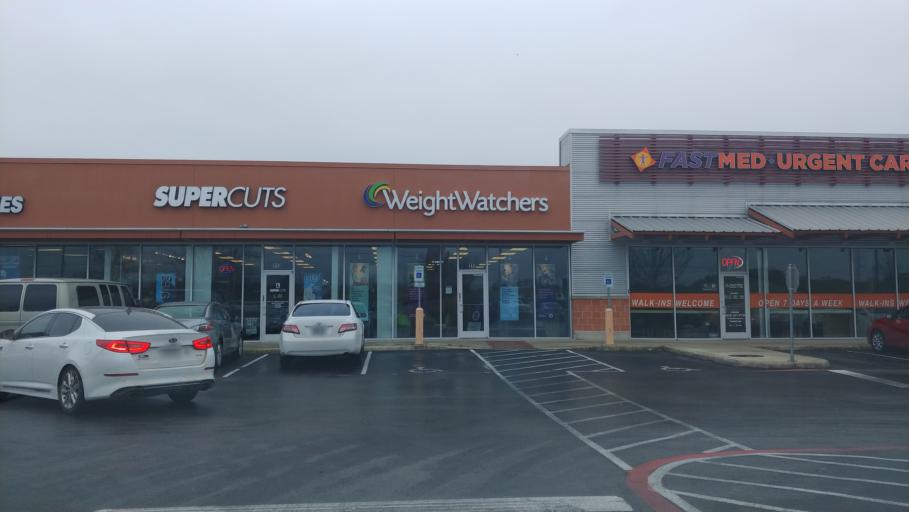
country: US
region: Texas
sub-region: Bexar County
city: Helotes
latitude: 29.5552
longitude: -98.6639
